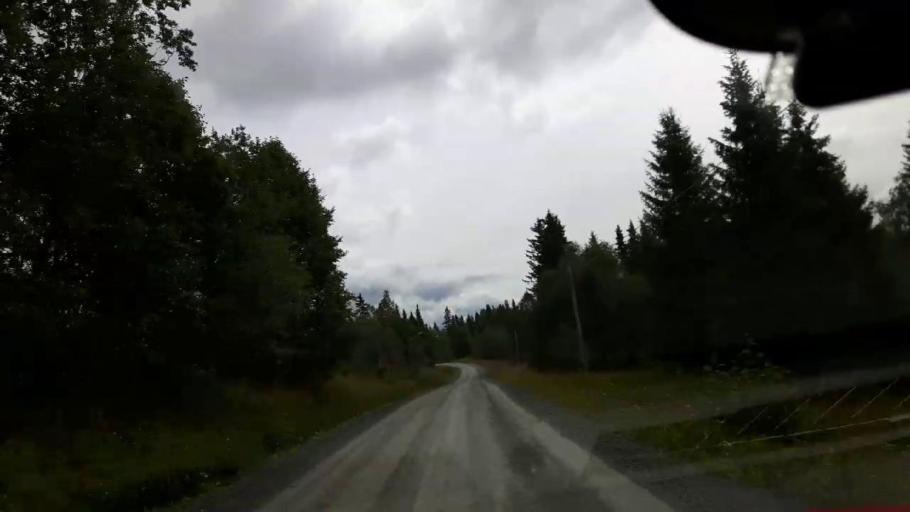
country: SE
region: Jaemtland
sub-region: Krokoms Kommun
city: Valla
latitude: 63.6732
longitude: 13.9493
